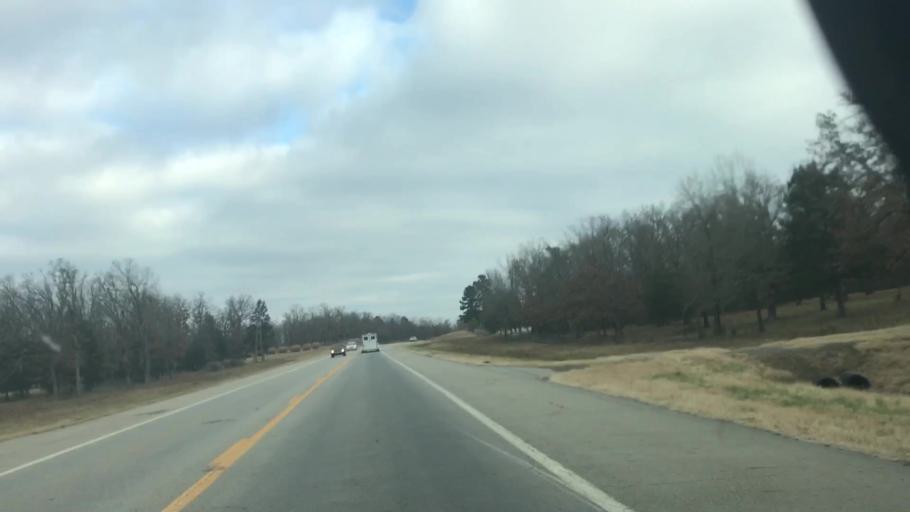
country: US
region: Arkansas
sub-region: Scott County
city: Waldron
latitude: 34.9192
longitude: -94.1071
